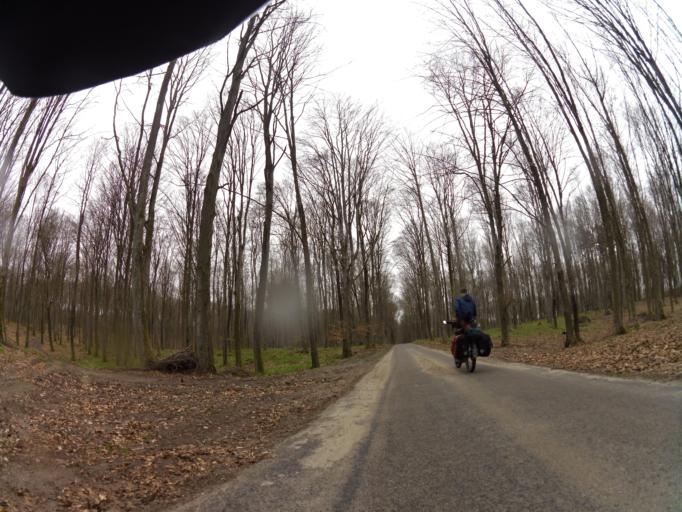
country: PL
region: West Pomeranian Voivodeship
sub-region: Powiat koszalinski
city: Bobolice
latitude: 53.9515
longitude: 16.6700
